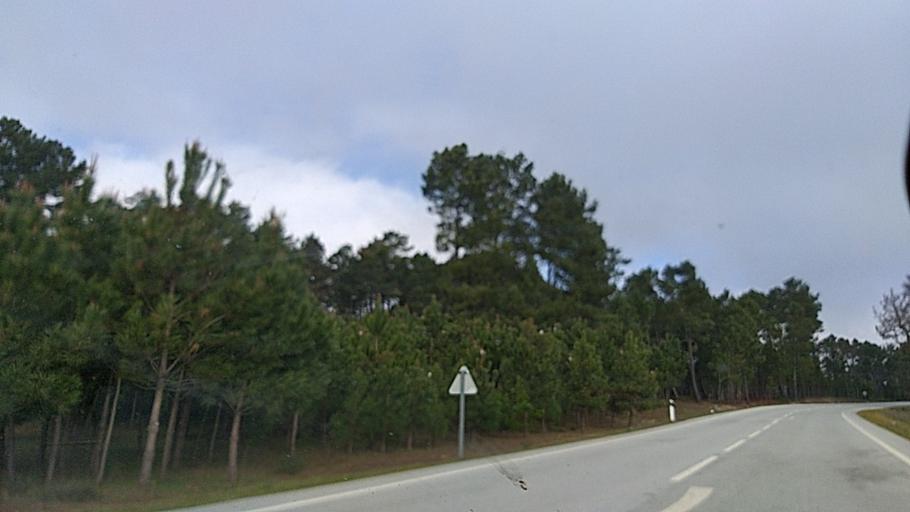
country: PT
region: Guarda
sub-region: Aguiar da Beira
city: Aguiar da Beira
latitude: 40.7492
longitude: -7.5045
